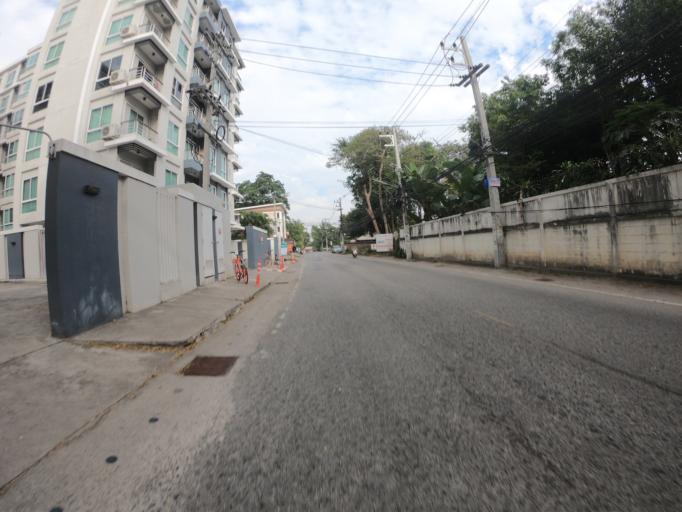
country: TH
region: Chiang Mai
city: Chiang Mai
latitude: 18.8129
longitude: 98.9770
